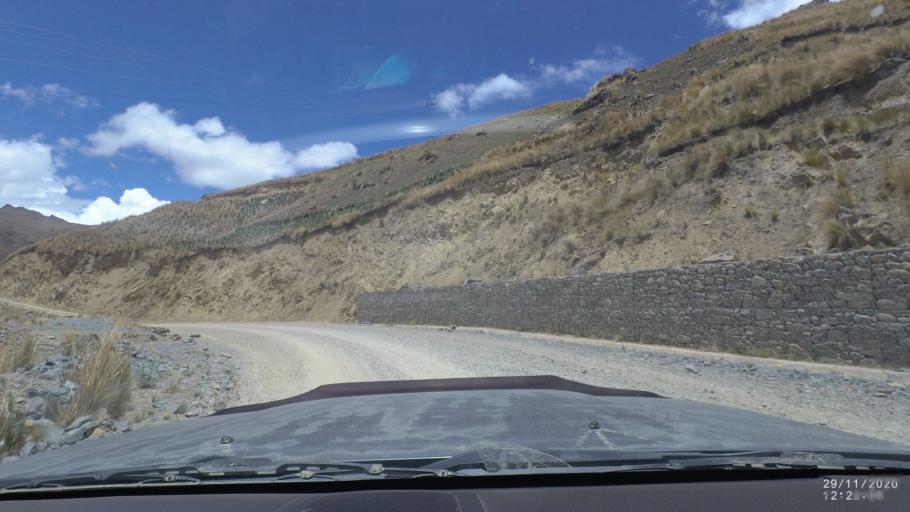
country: BO
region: Cochabamba
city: Cochabamba
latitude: -17.0972
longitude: -66.3264
